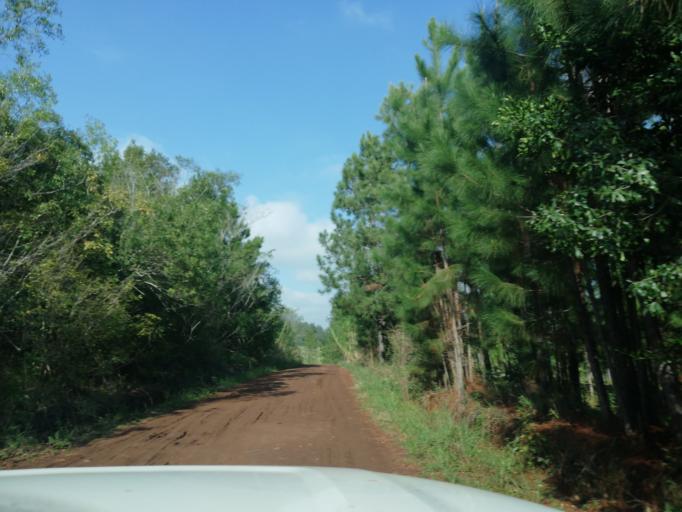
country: AR
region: Misiones
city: Cerro Azul
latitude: -27.5890
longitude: -55.5142
